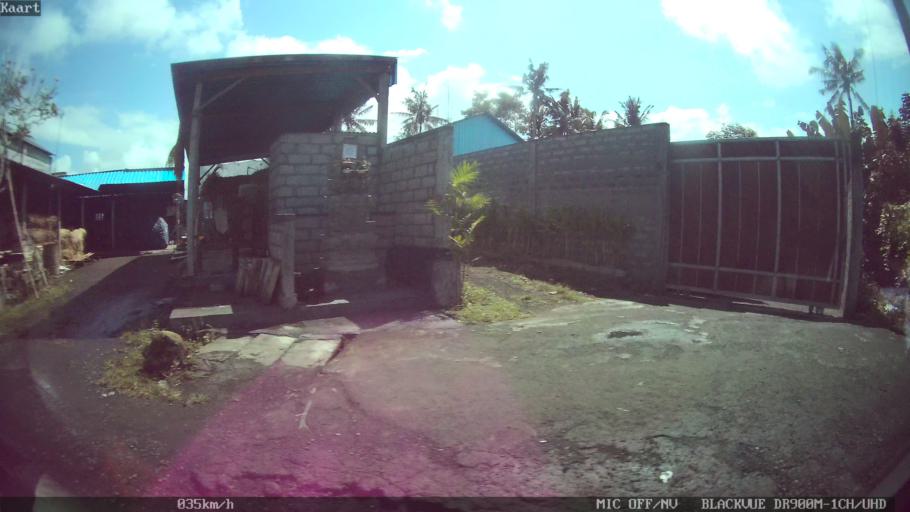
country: ID
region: Bali
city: Banjar Sedang
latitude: -8.5605
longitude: 115.2672
